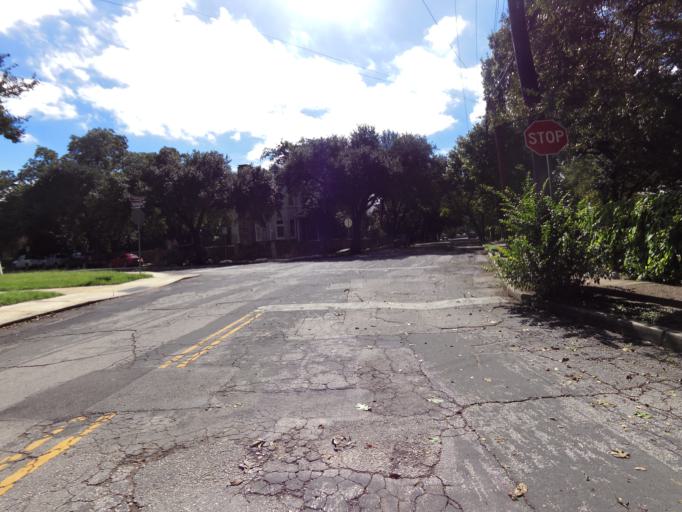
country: US
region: Texas
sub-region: Bexar County
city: San Antonio
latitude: 29.4173
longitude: -98.4922
